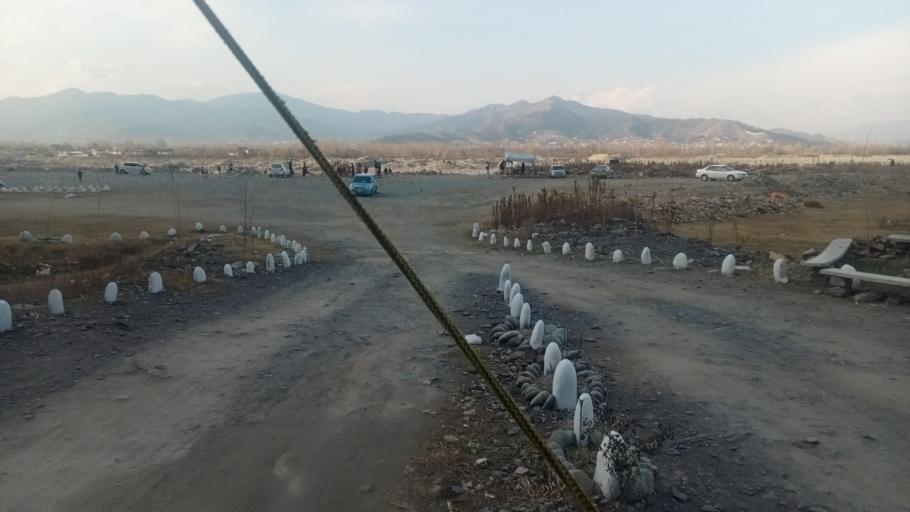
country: PK
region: Khyber Pakhtunkhwa
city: Mingora
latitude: 34.7919
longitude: 72.3901
